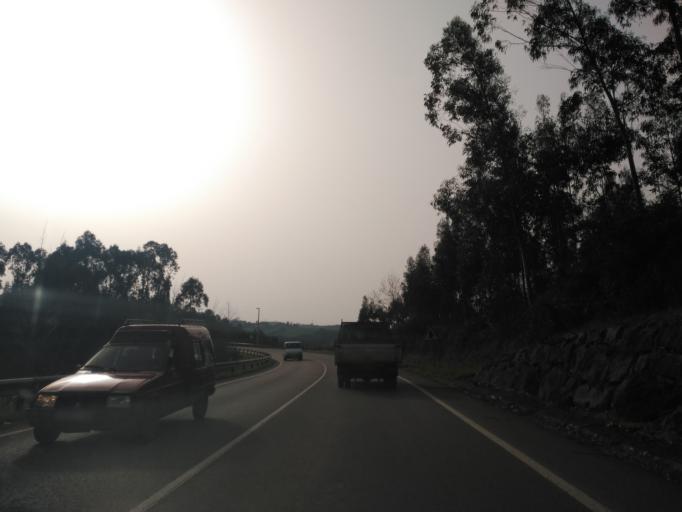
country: ES
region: Cantabria
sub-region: Provincia de Cantabria
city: Comillas
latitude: 43.3667
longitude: -4.2769
